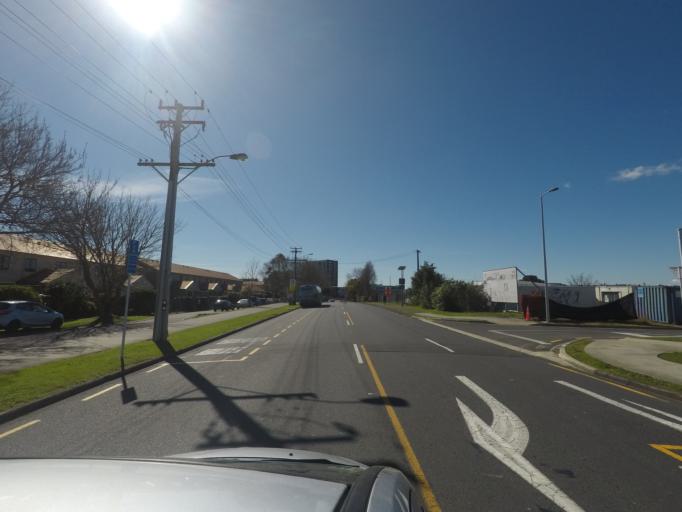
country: NZ
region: Auckland
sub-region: Auckland
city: Waitakere
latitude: -36.9130
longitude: 174.6817
